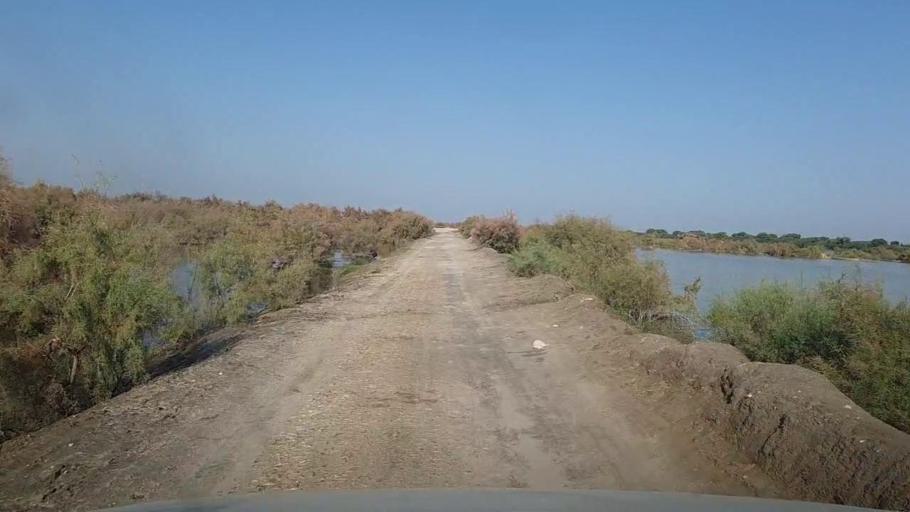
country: PK
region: Sindh
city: Kandhkot
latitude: 28.2814
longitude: 69.3286
